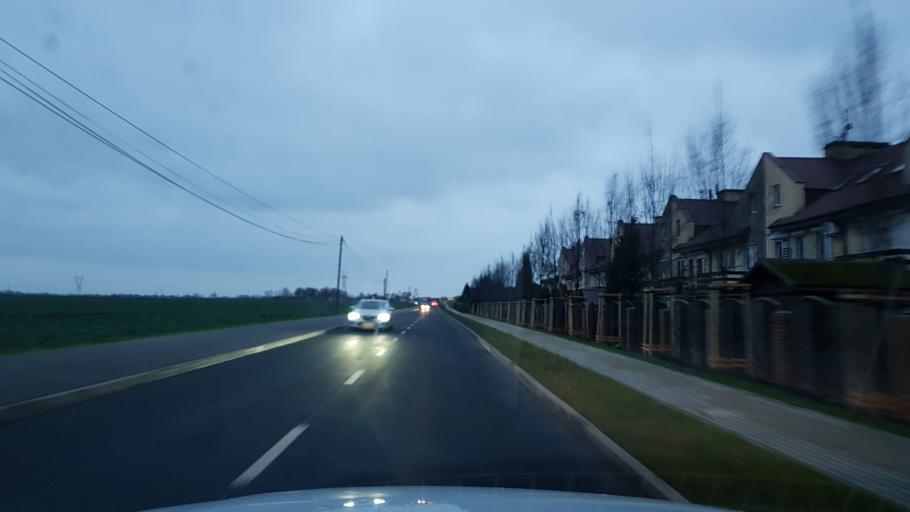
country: PL
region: West Pomeranian Voivodeship
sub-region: Powiat policki
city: Przeclaw
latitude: 53.4175
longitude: 14.4682
